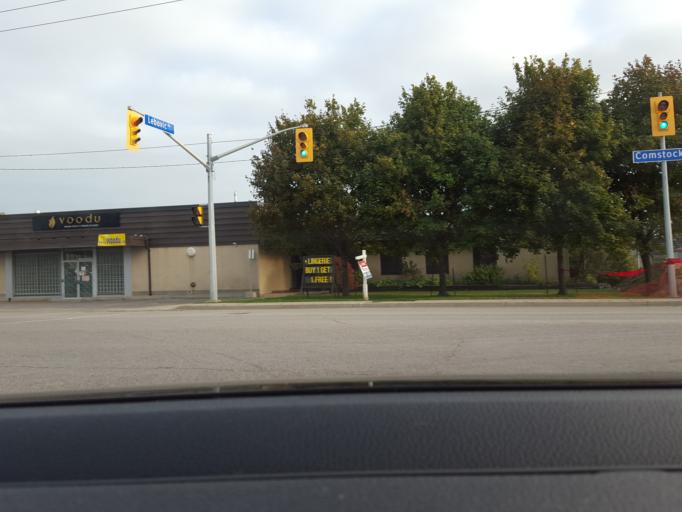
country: CA
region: Ontario
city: Scarborough
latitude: 43.7208
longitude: -79.2888
